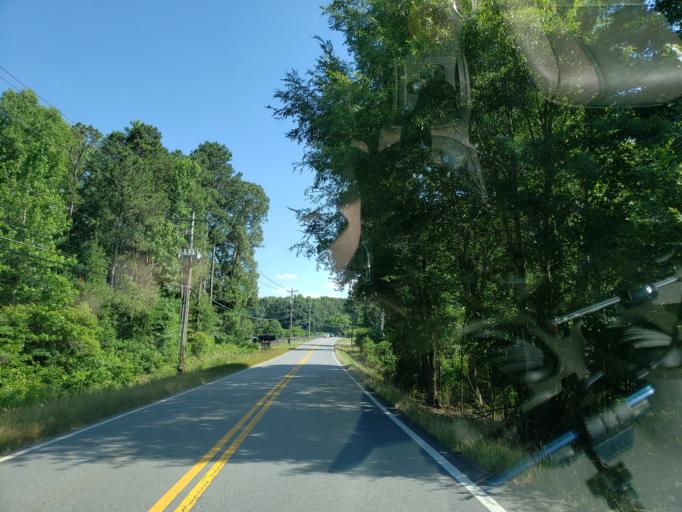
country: US
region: Georgia
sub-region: Cherokee County
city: Holly Springs
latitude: 34.1181
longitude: -84.4237
